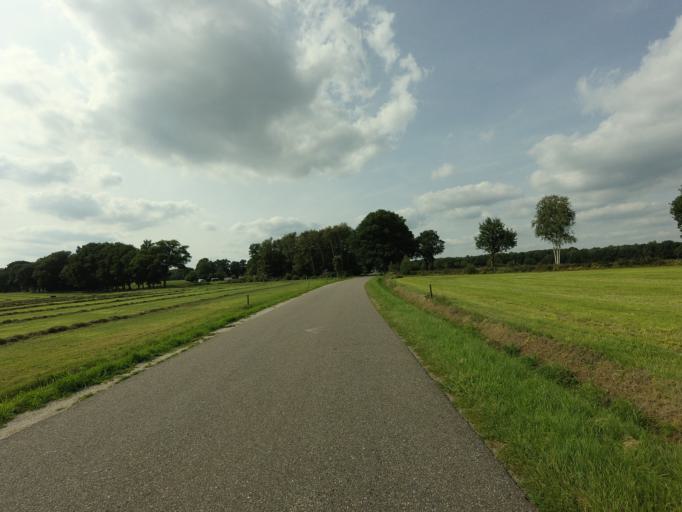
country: DE
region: Lower Saxony
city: Getelo
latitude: 52.4258
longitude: 6.8865
